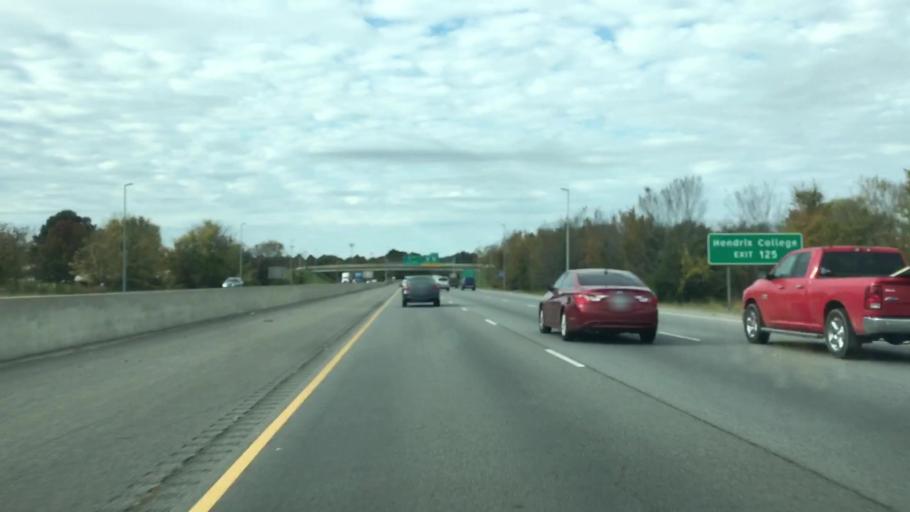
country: US
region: Arkansas
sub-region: Faulkner County
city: Conway
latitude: 35.0968
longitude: -92.4279
